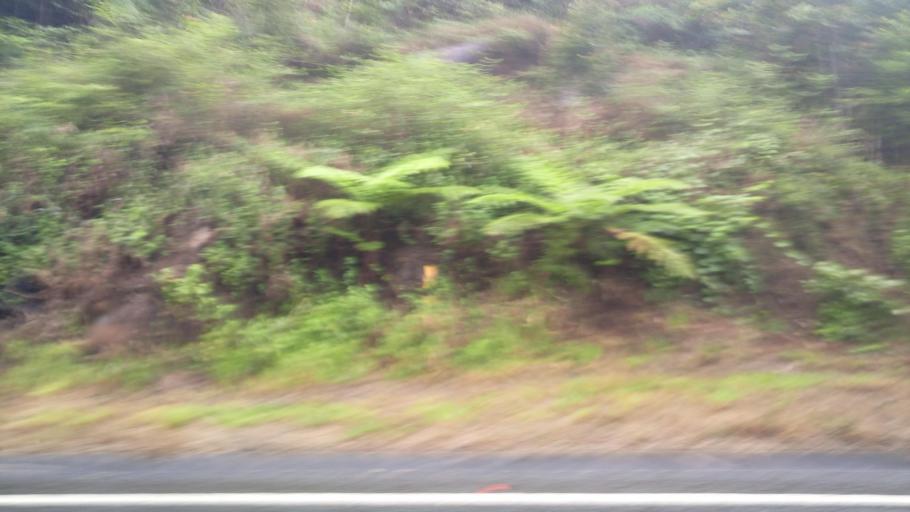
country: AU
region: Queensland
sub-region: Tablelands
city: Ravenshoe
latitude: -17.5693
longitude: 145.6843
